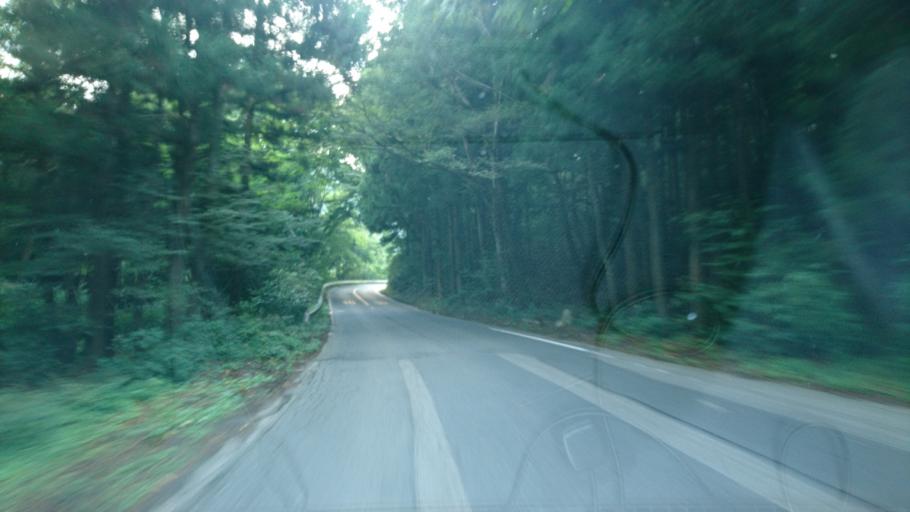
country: JP
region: Gunma
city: Numata
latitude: 36.6345
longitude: 139.1705
